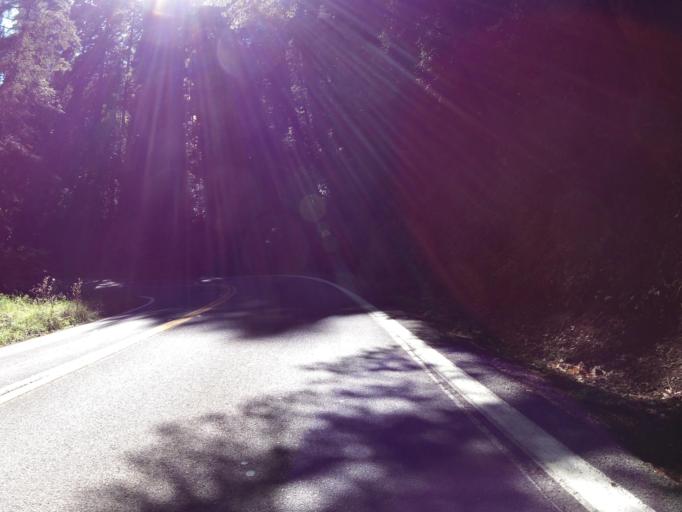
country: US
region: California
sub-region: Mendocino County
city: Fort Bragg
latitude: 39.7339
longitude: -123.8104
